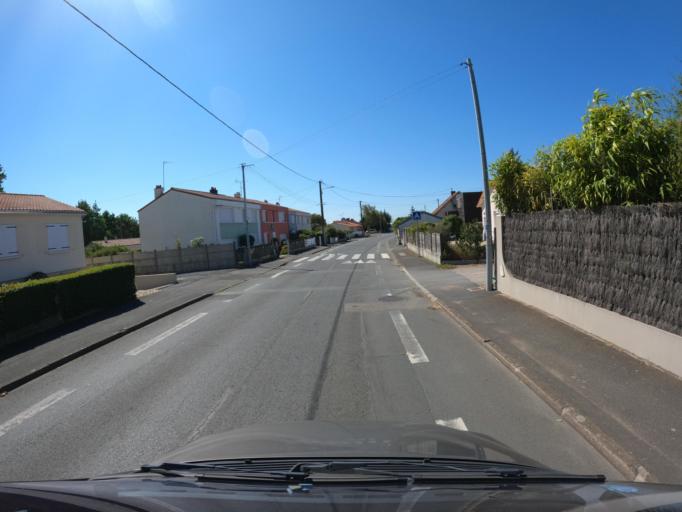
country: FR
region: Pays de la Loire
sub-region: Departement de la Vendee
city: Montaigu
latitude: 46.9682
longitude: -1.3030
